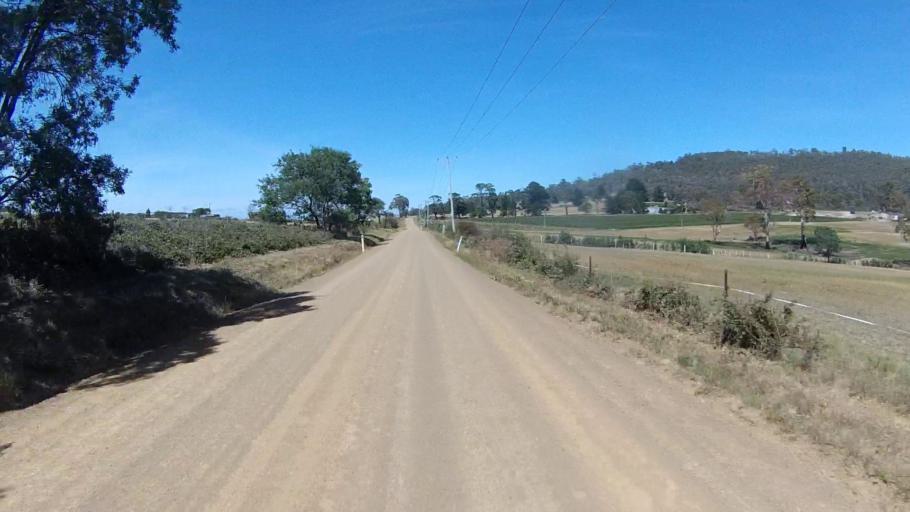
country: AU
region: Tasmania
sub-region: Sorell
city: Sorell
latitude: -42.7841
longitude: 147.6390
